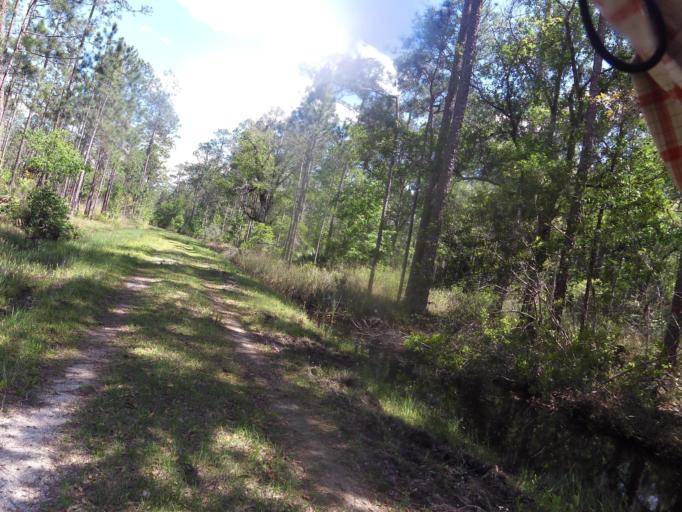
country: US
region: Florida
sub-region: Clay County
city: Green Cove Springs
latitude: 29.9659
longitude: -81.6393
